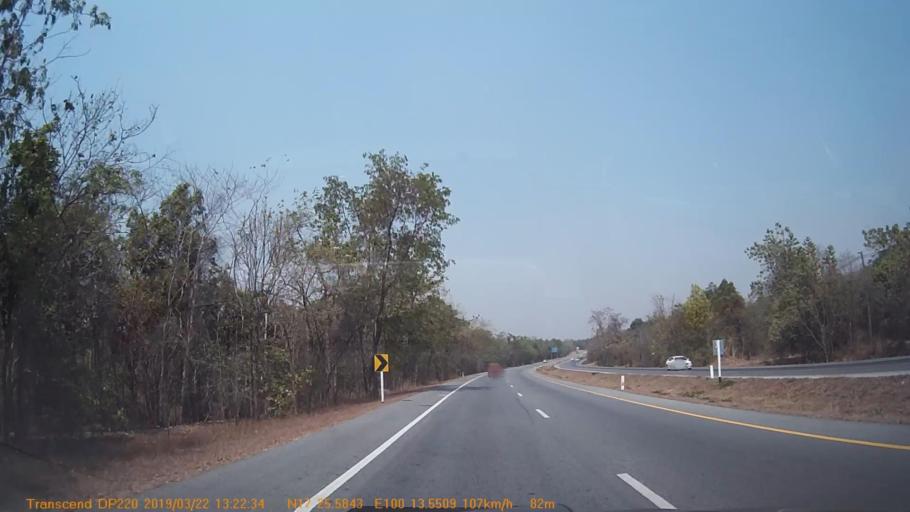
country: TH
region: Uttaradit
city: Thong Saen Khan
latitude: 17.4266
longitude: 100.2259
